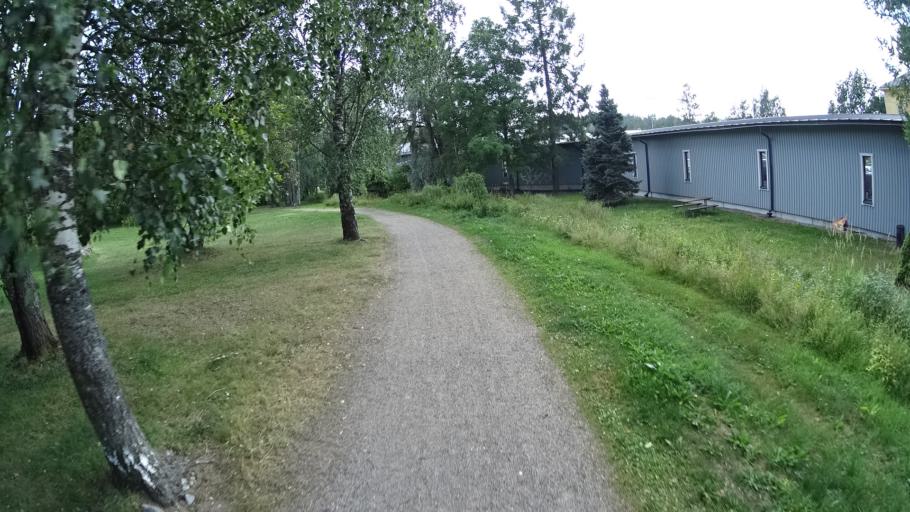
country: FI
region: Uusimaa
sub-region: Porvoo
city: Porvoo
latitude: 60.3855
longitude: 25.6713
